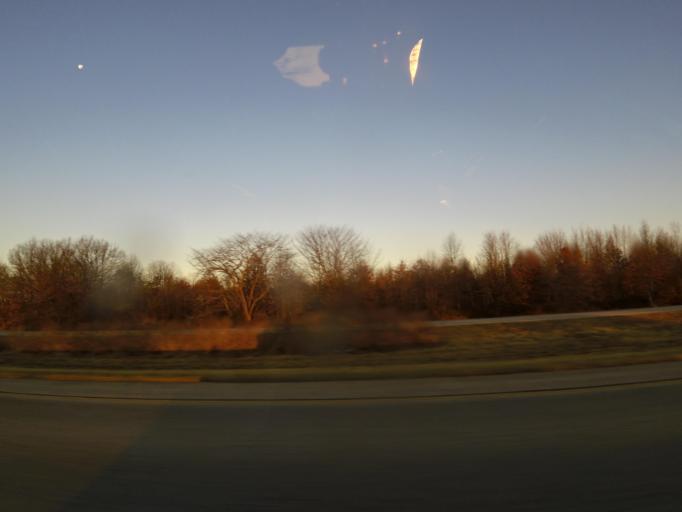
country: US
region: Illinois
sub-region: Marion County
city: Salem
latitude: 38.7001
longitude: -88.9559
